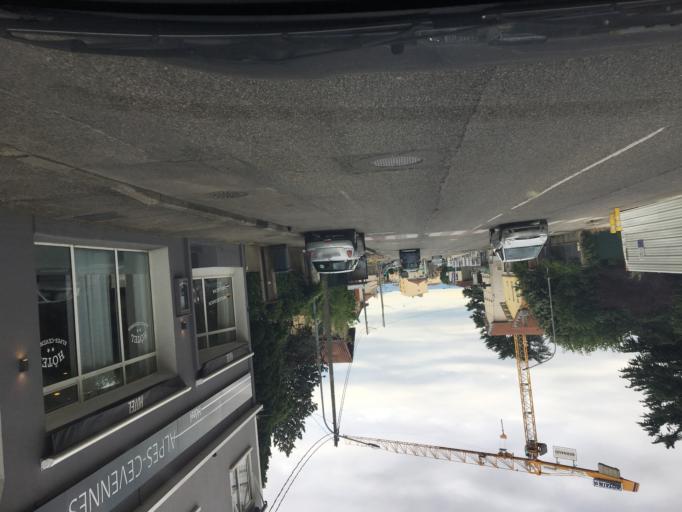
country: FR
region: Rhone-Alpes
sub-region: Departement de l'Ardeche
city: Guilherand-Granges
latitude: 44.9354
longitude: 4.8751
